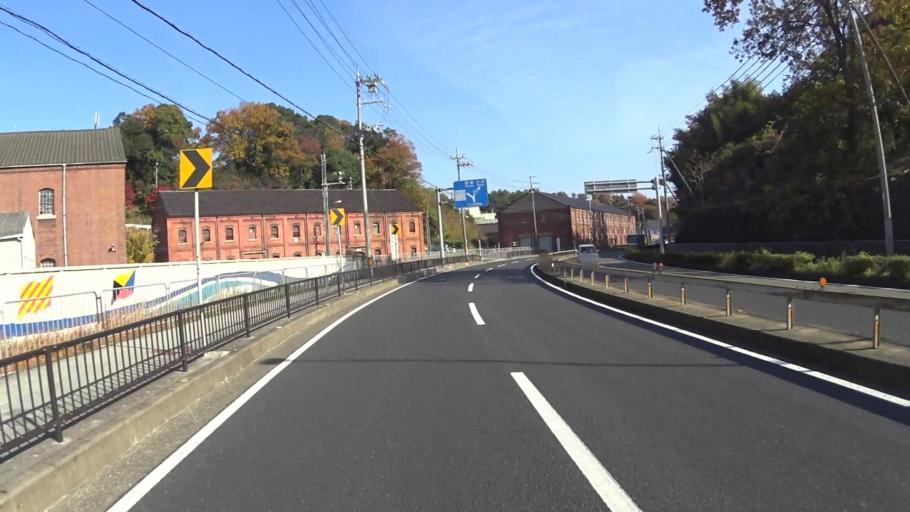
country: JP
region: Kyoto
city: Maizuru
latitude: 35.4742
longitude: 135.3827
